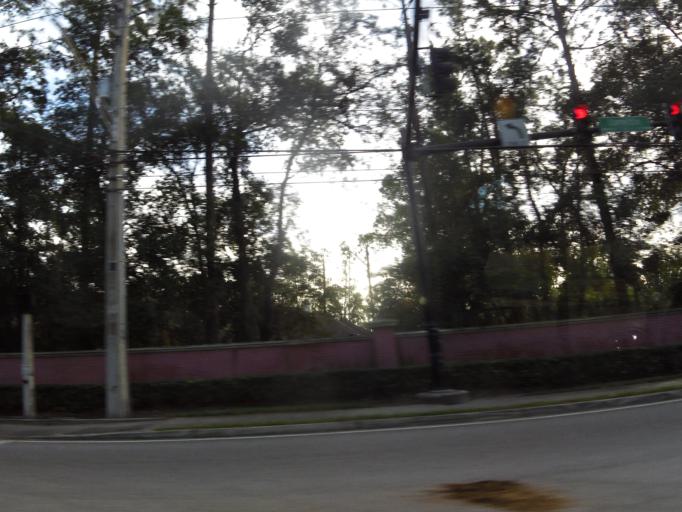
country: US
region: Florida
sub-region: Saint Johns County
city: Fruit Cove
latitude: 30.1590
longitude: -81.6112
